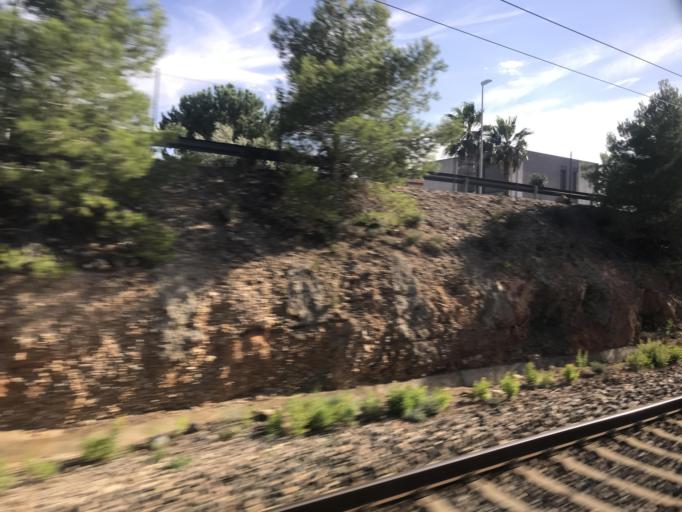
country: ES
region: Catalonia
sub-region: Provincia de Tarragona
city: L'Ampolla
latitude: 40.8234
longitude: 0.7272
